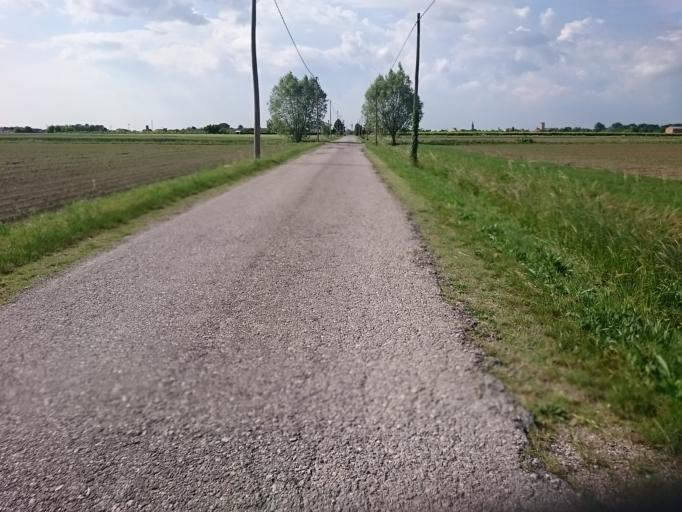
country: IT
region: Veneto
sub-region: Provincia di Padova
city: Montagnana
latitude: 45.2175
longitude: 11.4749
